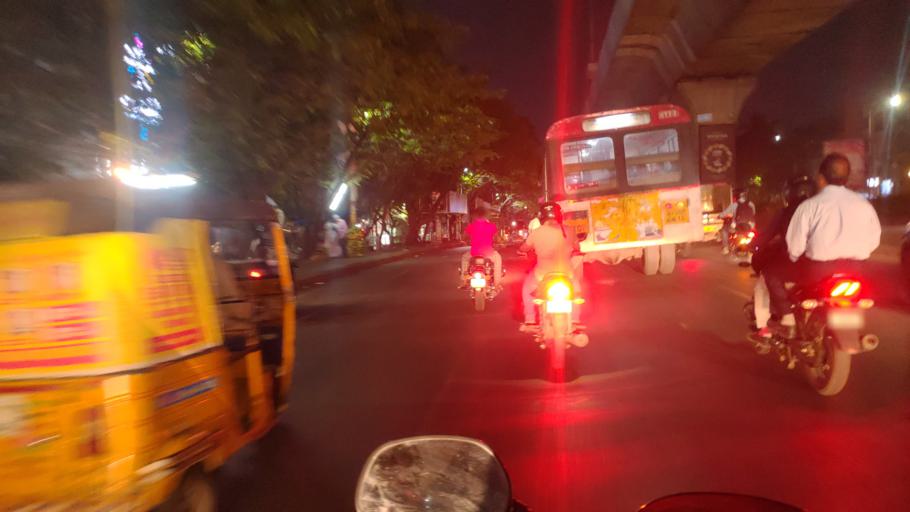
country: IN
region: Telangana
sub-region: Rangareddi
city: Gaddi Annaram
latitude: 17.3698
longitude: 78.5159
